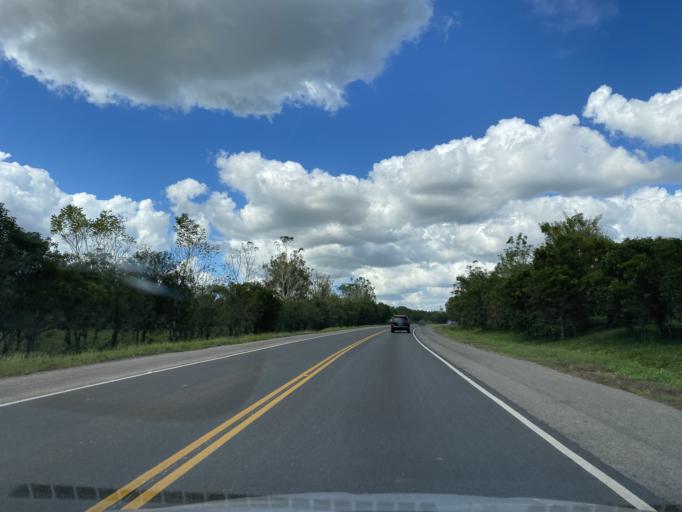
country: DO
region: Monte Plata
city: Monte Plata
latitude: 18.7184
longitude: -69.7593
